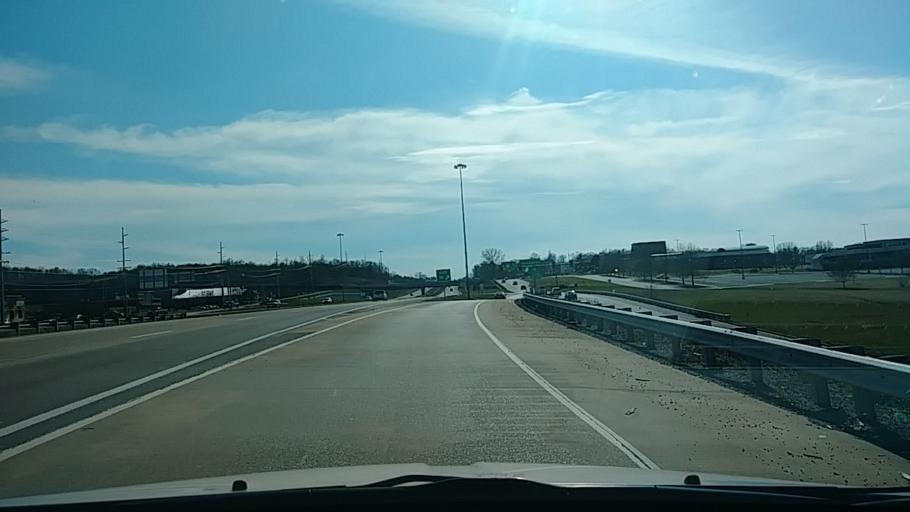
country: US
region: Tennessee
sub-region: Hamblen County
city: Morristown
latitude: 36.2168
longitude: -83.2574
